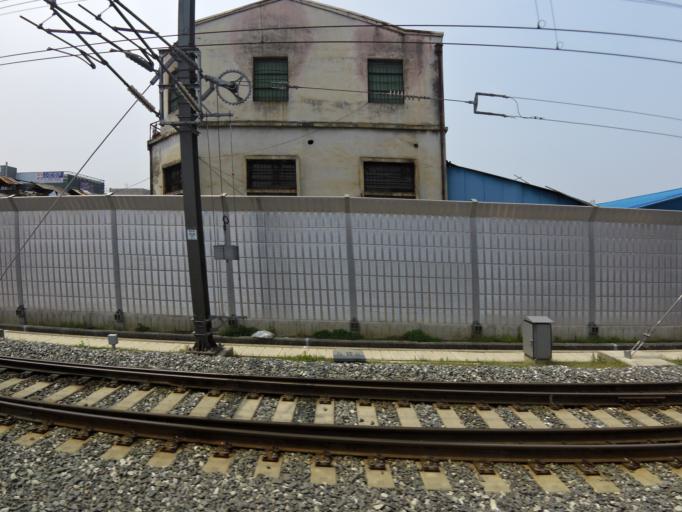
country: KR
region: Daejeon
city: Daejeon
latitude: 36.3278
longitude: 127.4363
